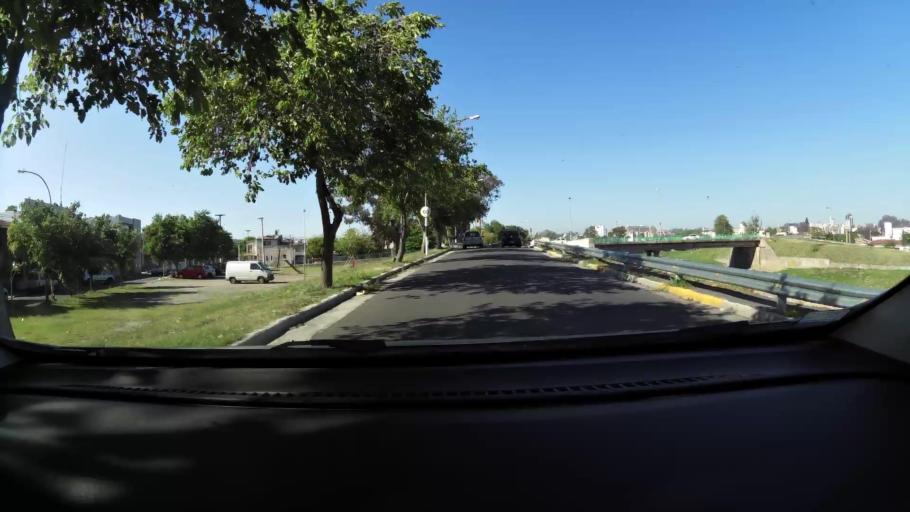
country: AR
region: Cordoba
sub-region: Departamento de Capital
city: Cordoba
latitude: -31.4205
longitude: -64.1580
